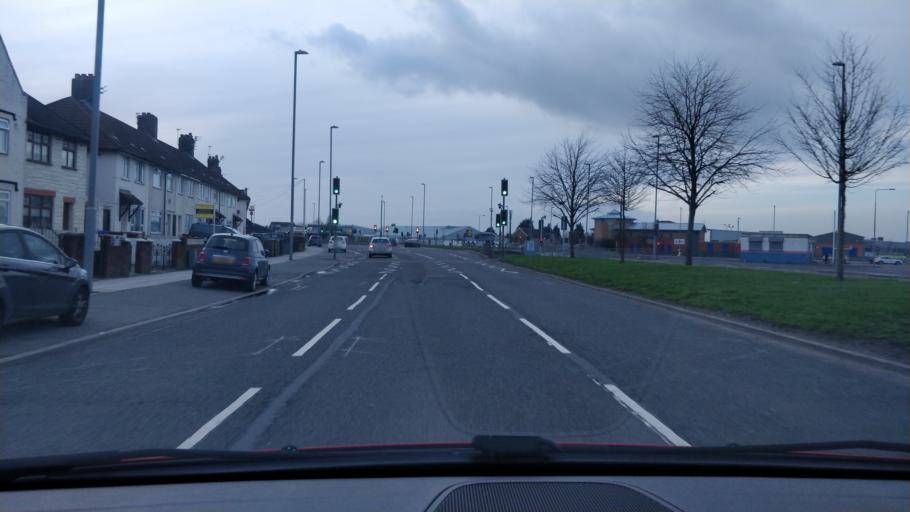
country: GB
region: England
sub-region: Knowsley
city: Huyton
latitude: 53.4215
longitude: -2.8583
